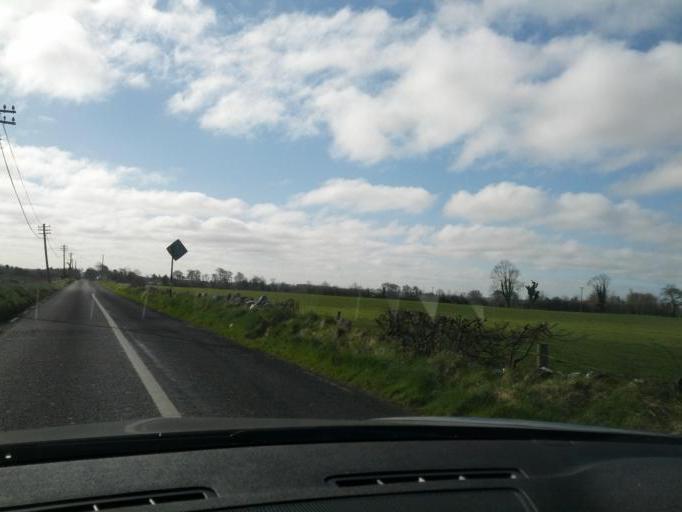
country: IE
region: Connaught
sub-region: County Galway
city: Ballinasloe
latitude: 53.3668
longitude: -8.2606
